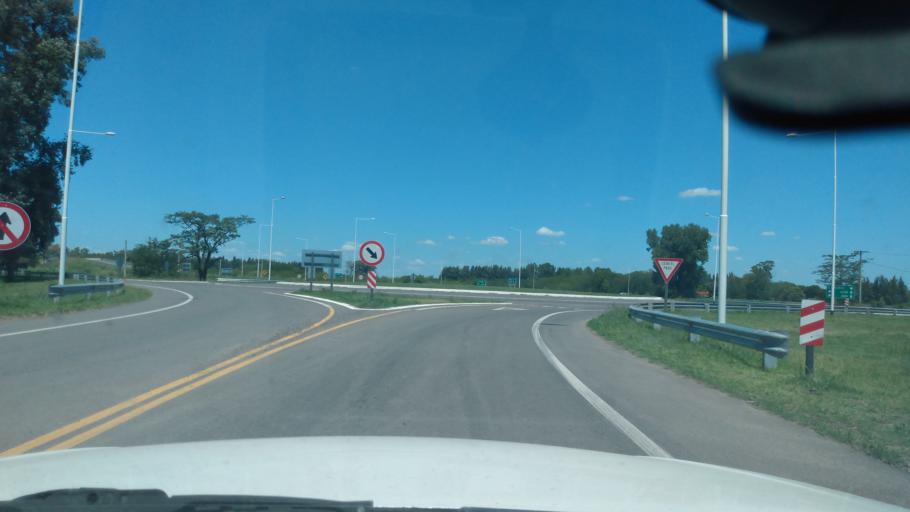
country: AR
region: Buenos Aires
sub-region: Partido de San Andres de Giles
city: San Andres de Giles
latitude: -34.4587
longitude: -59.4174
